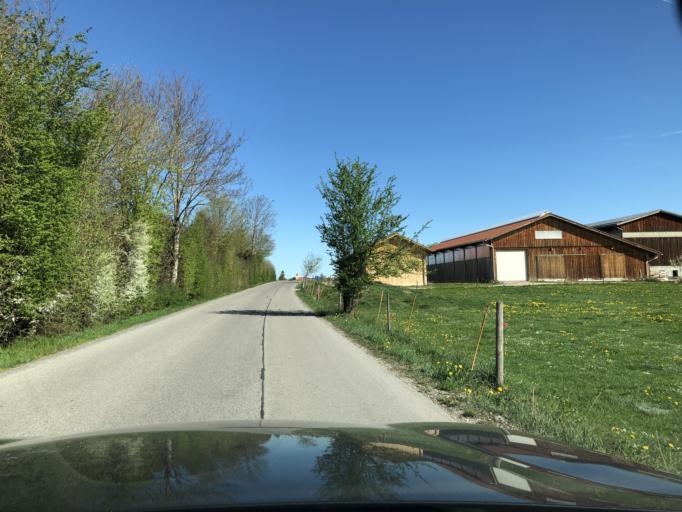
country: DE
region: Bavaria
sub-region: Swabia
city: Wald
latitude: 47.7565
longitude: 10.5692
